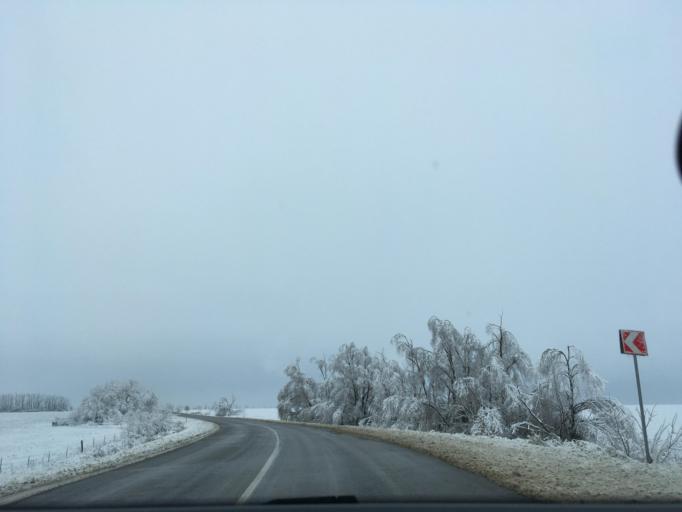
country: RU
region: Voronezj
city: Ol'khovatka
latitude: 50.2216
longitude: 39.2753
